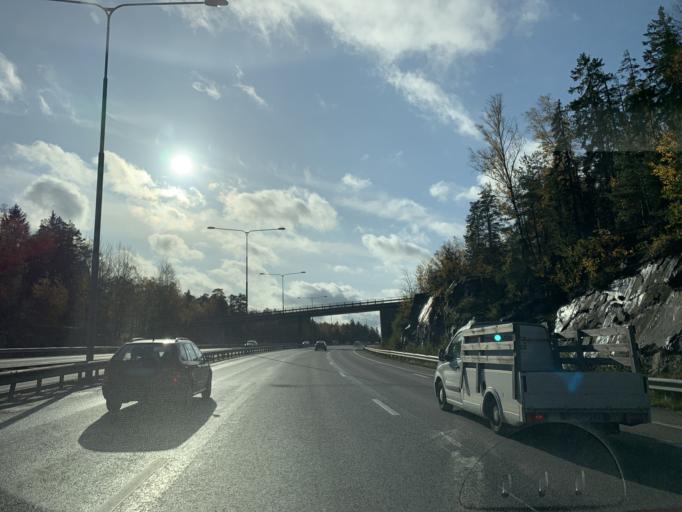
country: SE
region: Stockholm
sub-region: Haninge Kommun
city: Handen
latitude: 59.2164
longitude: 18.1347
